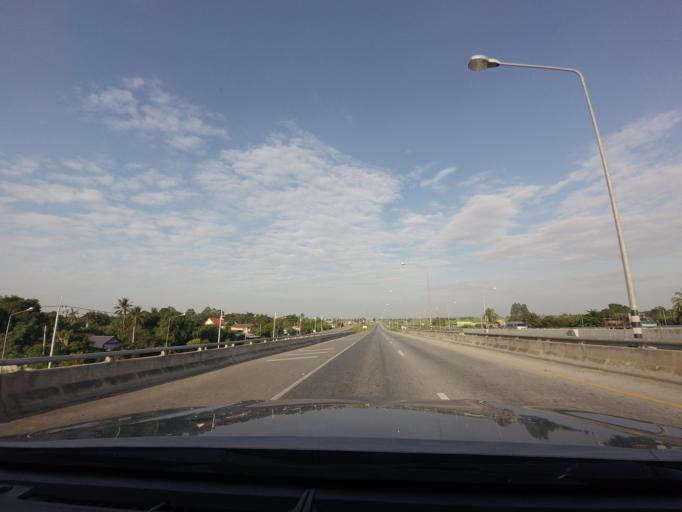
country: TH
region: Nakhon Sawan
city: Nakhon Sawan
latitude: 15.7546
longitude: 100.0881
